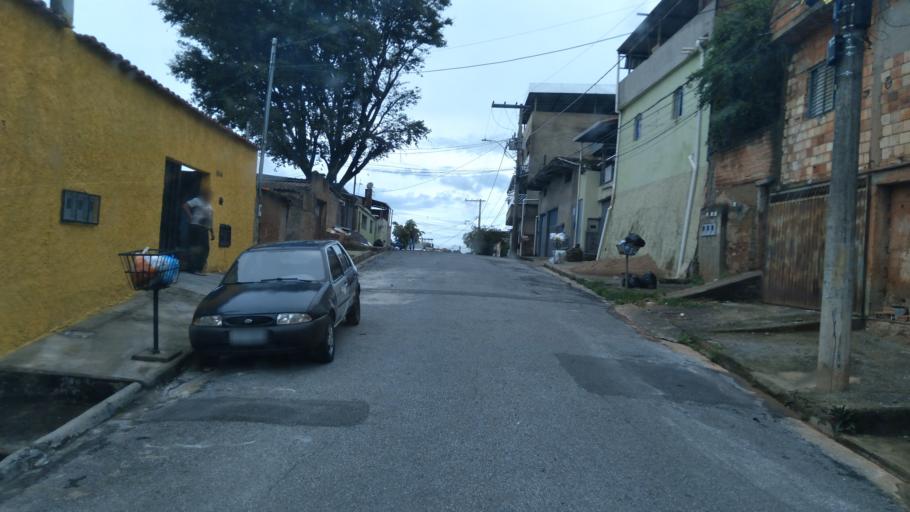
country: BR
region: Minas Gerais
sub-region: Contagem
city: Contagem
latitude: -19.9076
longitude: -44.0159
